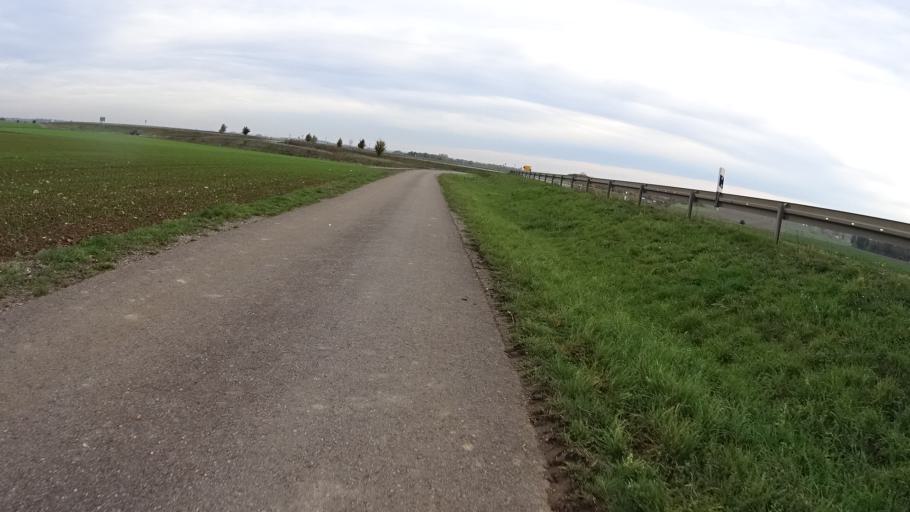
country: DE
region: Bavaria
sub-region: Upper Bavaria
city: Eitensheim
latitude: 48.8269
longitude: 11.3311
